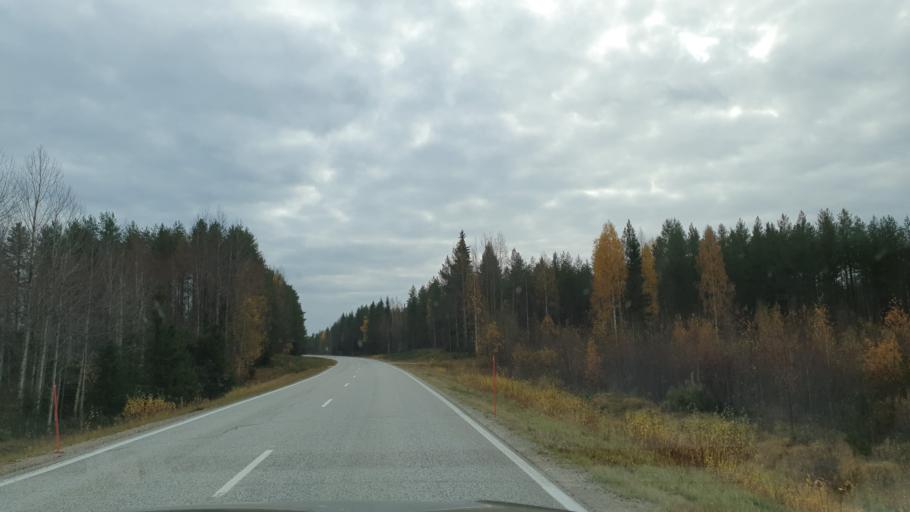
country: FI
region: Kainuu
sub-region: Kehys-Kainuu
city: Puolanka
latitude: 65.2437
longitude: 27.5812
